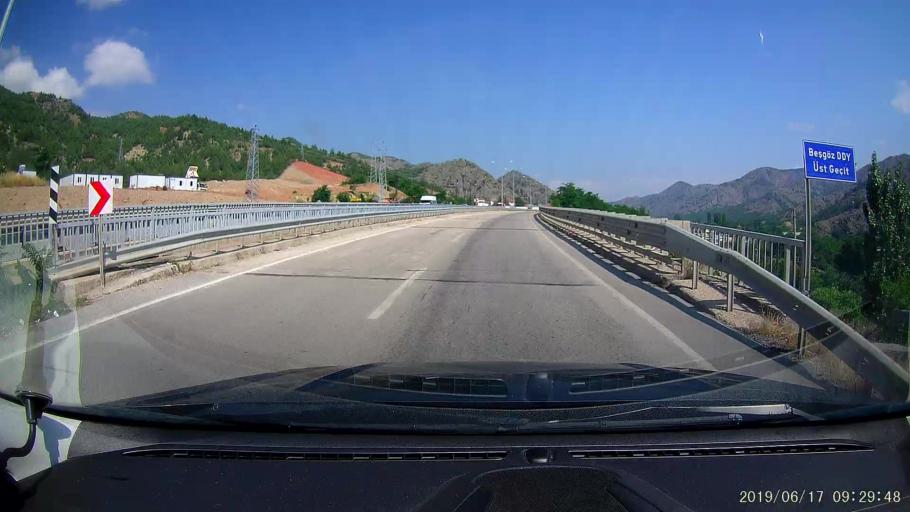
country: TR
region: Amasya
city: Amasya
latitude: 40.6993
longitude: 35.8077
